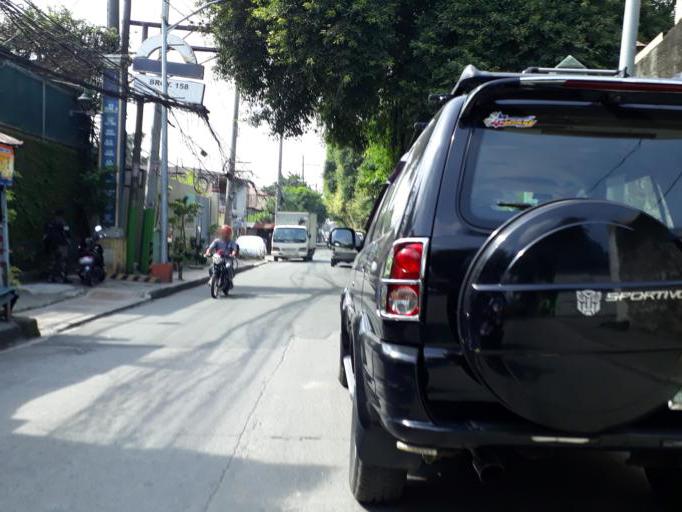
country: PH
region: Calabarzon
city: Bagong Pagasa
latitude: 14.6712
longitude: 121.0058
